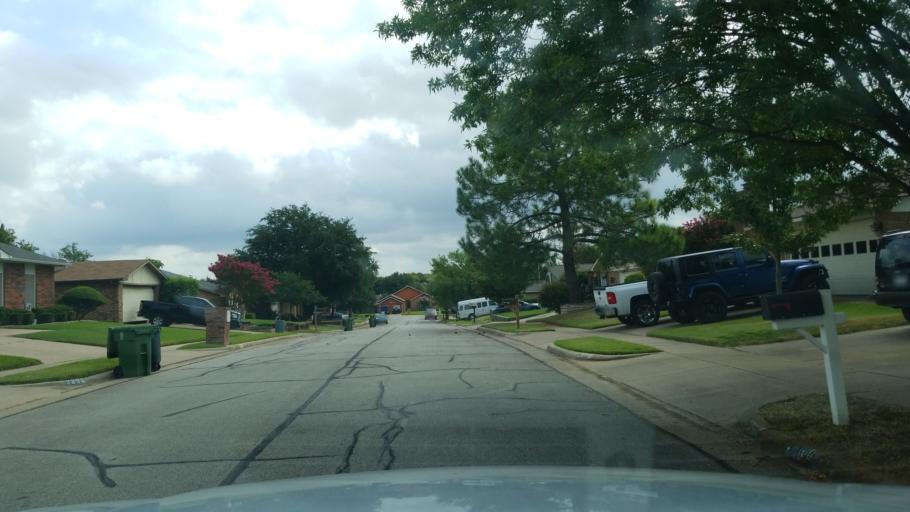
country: US
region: Texas
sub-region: Tarrant County
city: Euless
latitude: 32.8474
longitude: -97.1061
